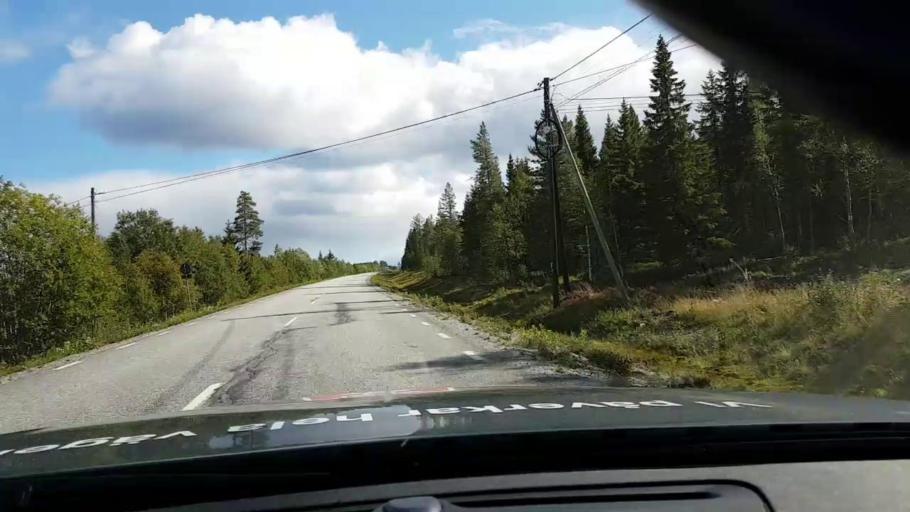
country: SE
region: Vaesterbotten
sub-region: Asele Kommun
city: Asele
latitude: 63.7811
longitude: 17.6628
